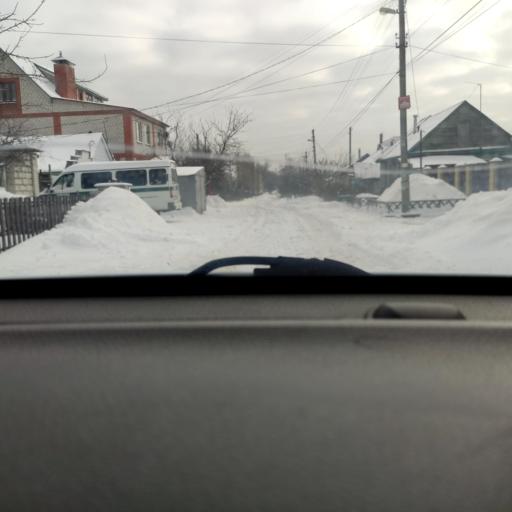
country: RU
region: Voronezj
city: Somovo
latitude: 51.7361
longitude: 39.2766
